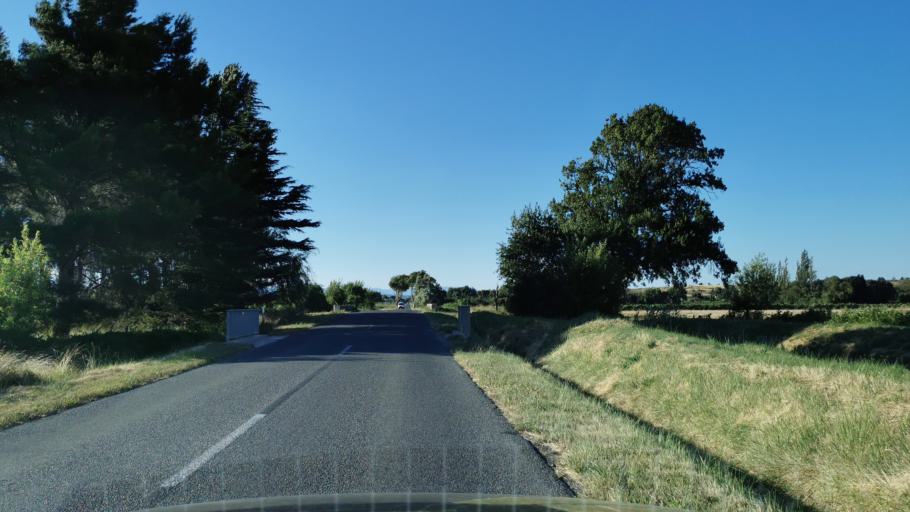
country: FR
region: Languedoc-Roussillon
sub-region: Departement de l'Aude
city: Ouveillan
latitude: 43.2585
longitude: 2.9961
